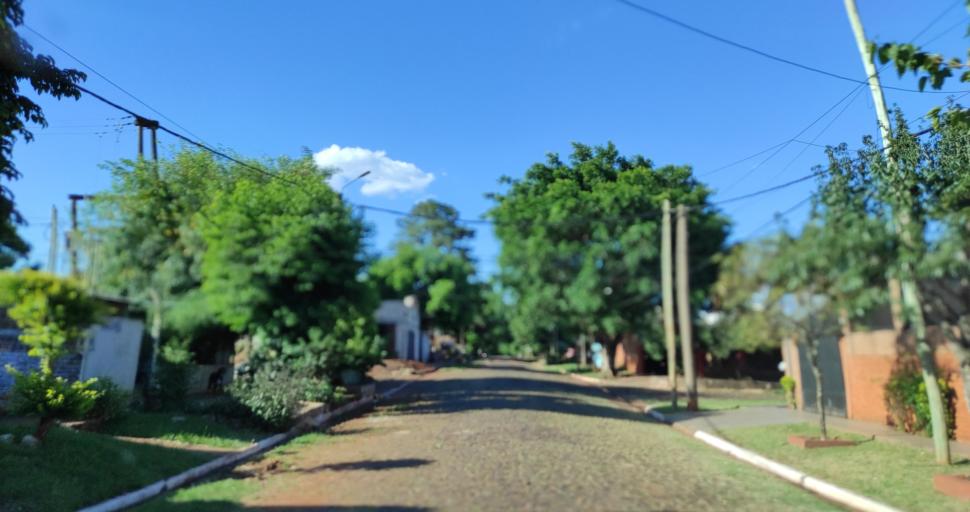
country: AR
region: Misiones
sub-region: Departamento de Capital
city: Posadas
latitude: -27.3803
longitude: -55.9241
